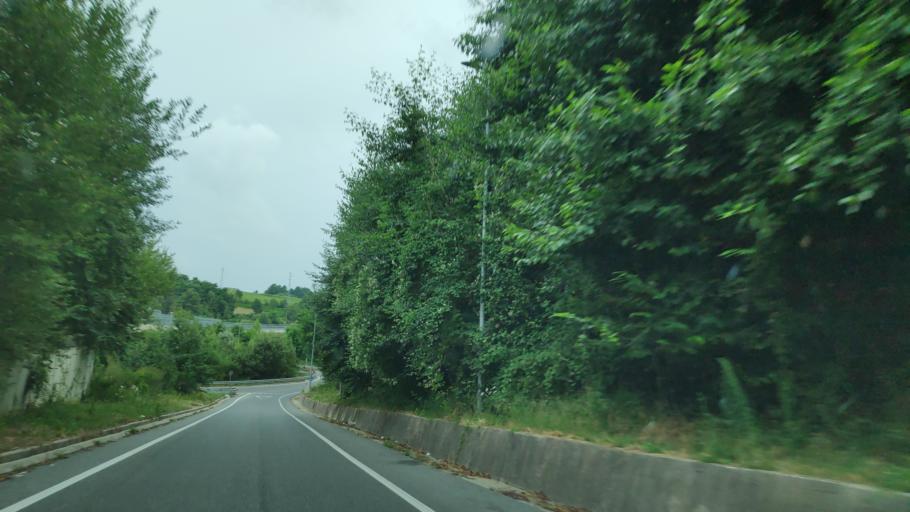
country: IT
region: Calabria
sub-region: Provincia di Vibo-Valentia
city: Spadola
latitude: 38.5938
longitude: 16.3311
